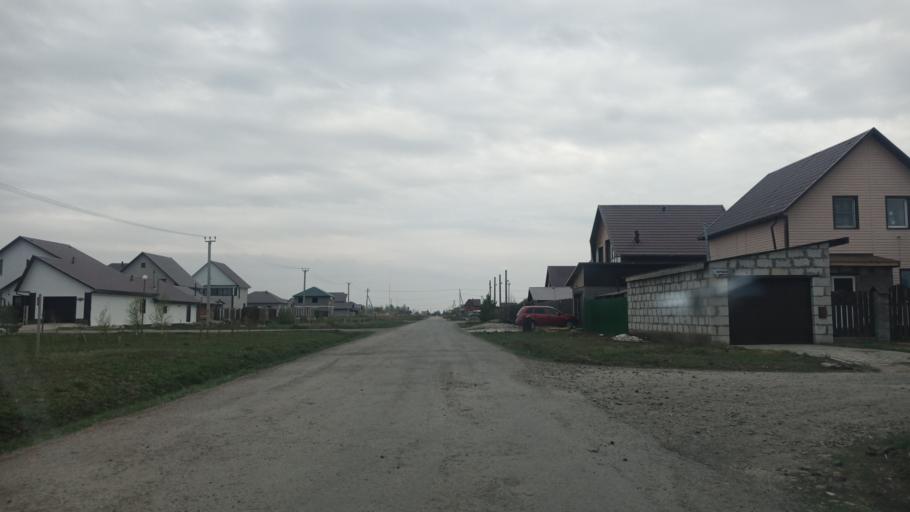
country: RU
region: Altai Krai
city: Yuzhnyy
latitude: 53.2227
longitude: 83.6916
